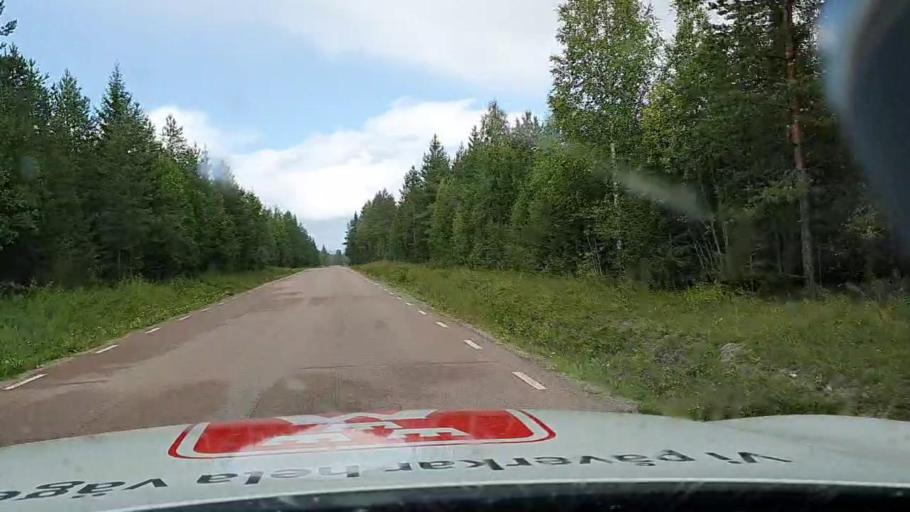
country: SE
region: Jaemtland
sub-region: Stroemsunds Kommun
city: Stroemsund
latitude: 63.8735
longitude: 15.3646
